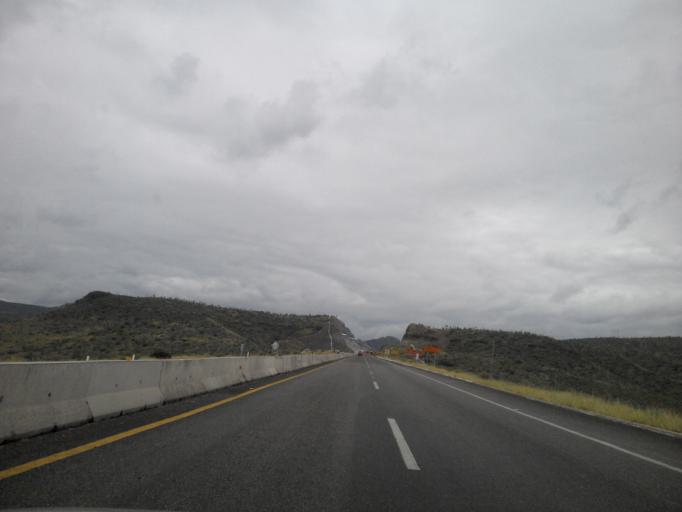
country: MX
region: Durango
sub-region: Lerdo
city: Picardias
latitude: 25.1779
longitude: -103.7175
